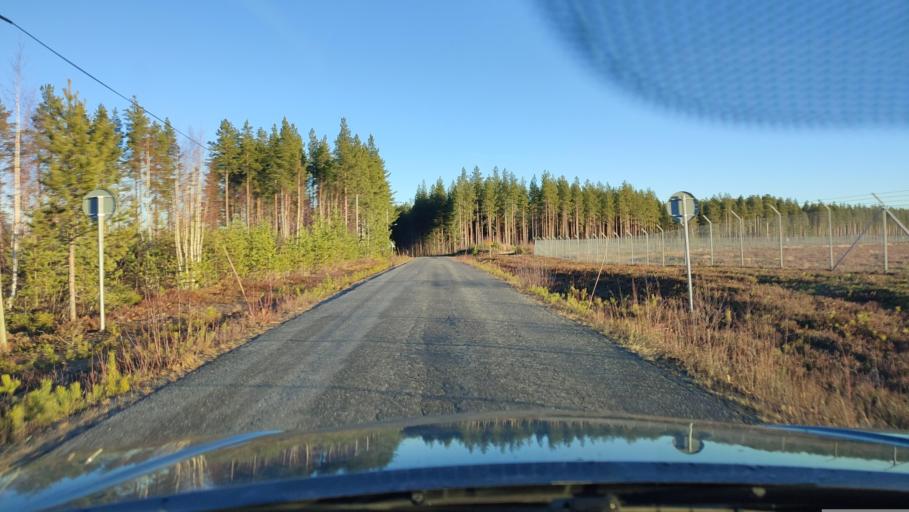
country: SE
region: Vaesterbotten
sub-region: Skelleftea Kommun
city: Soedra Bergsbyn
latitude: 64.6295
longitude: 21.0547
